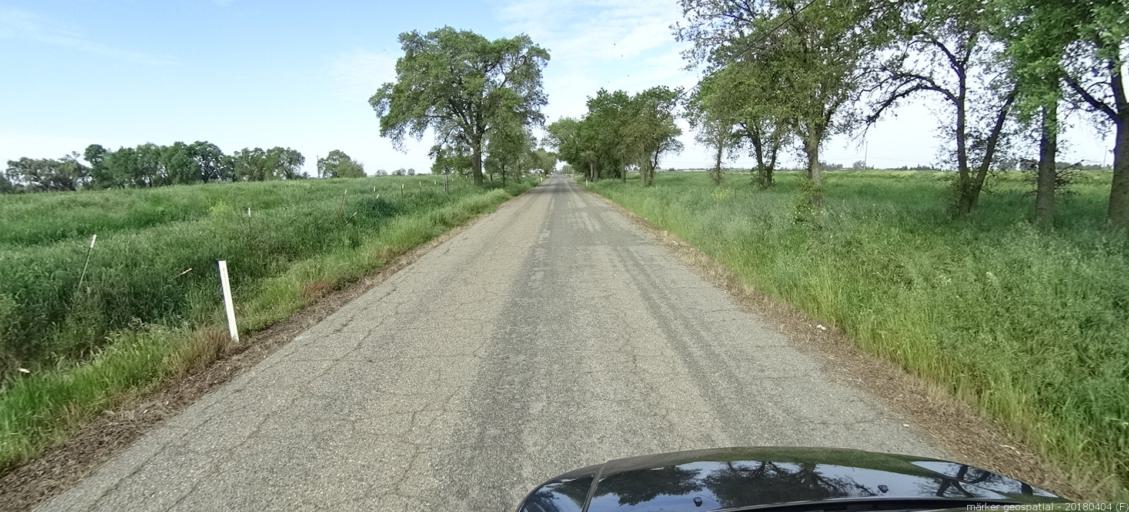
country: US
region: California
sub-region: Sacramento County
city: Herald
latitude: 38.2558
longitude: -121.2245
